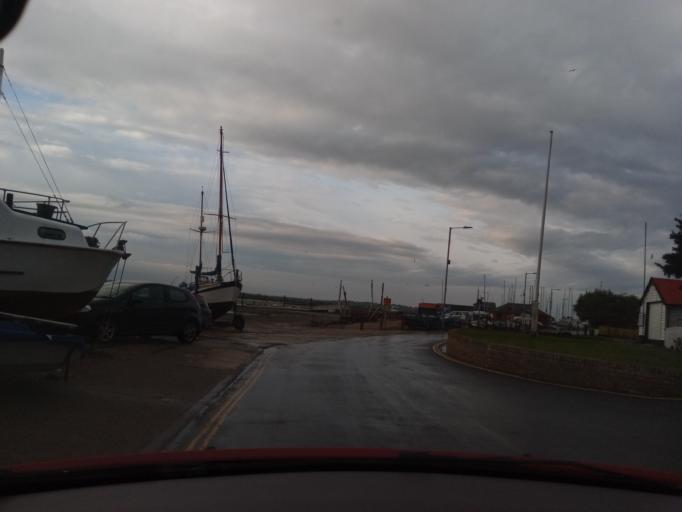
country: GB
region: England
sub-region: Essex
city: West Mersea
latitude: 51.7783
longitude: 0.8989
